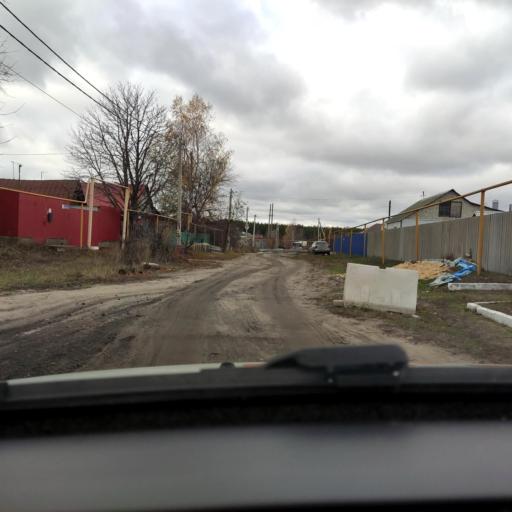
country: RU
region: Voronezj
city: Shilovo
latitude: 51.5216
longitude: 39.1484
